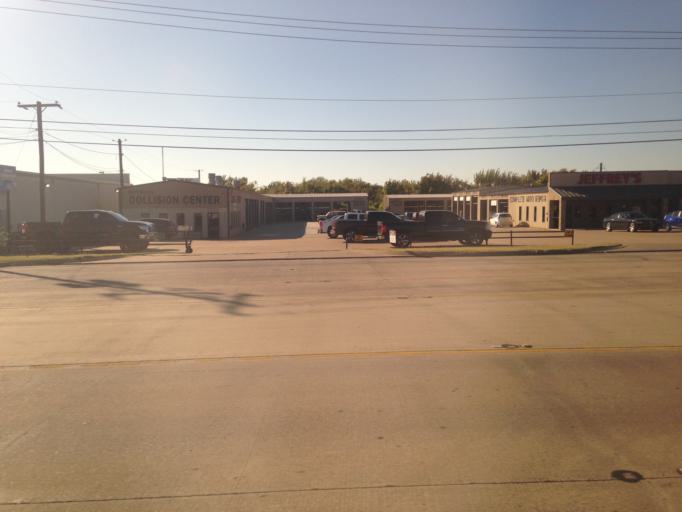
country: US
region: Texas
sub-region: Tarrant County
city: Watauga
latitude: 32.8545
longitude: -97.2640
